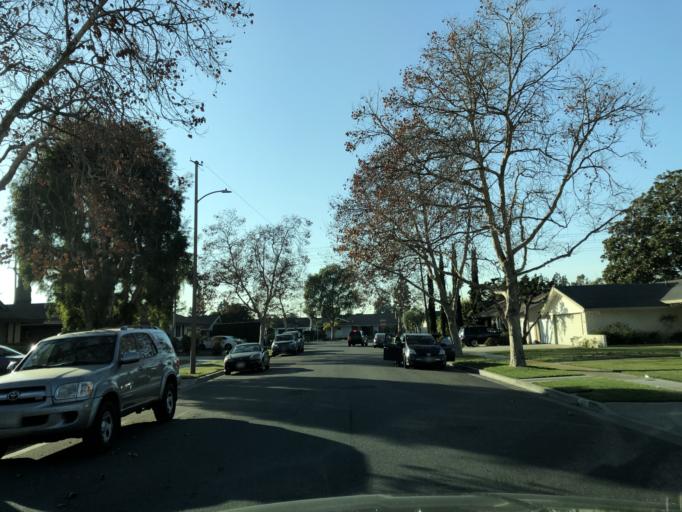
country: US
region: California
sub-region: Orange County
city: Orange
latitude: 33.7723
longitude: -117.8487
